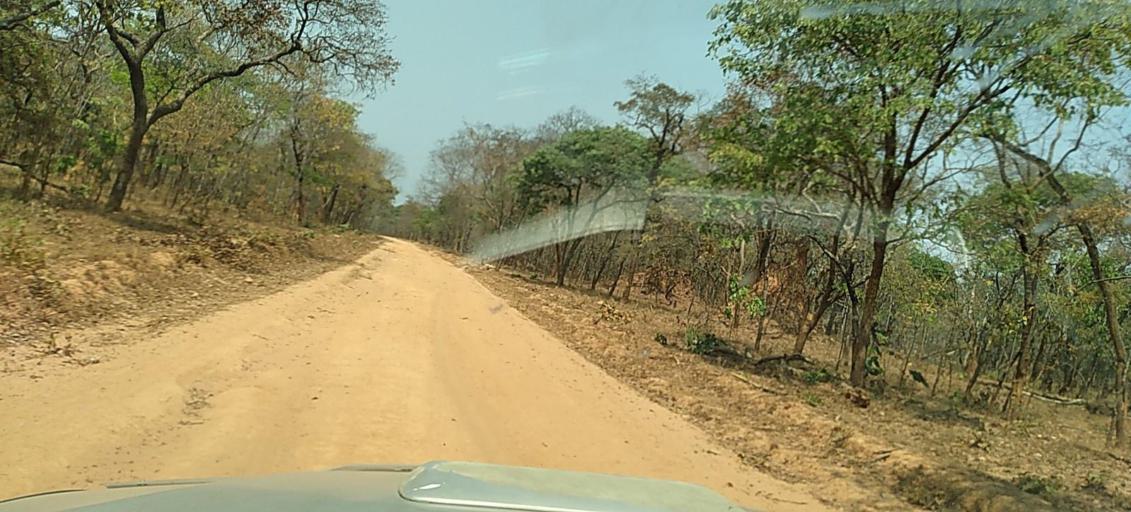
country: ZM
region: North-Western
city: Kasempa
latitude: -13.6635
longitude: 26.2776
